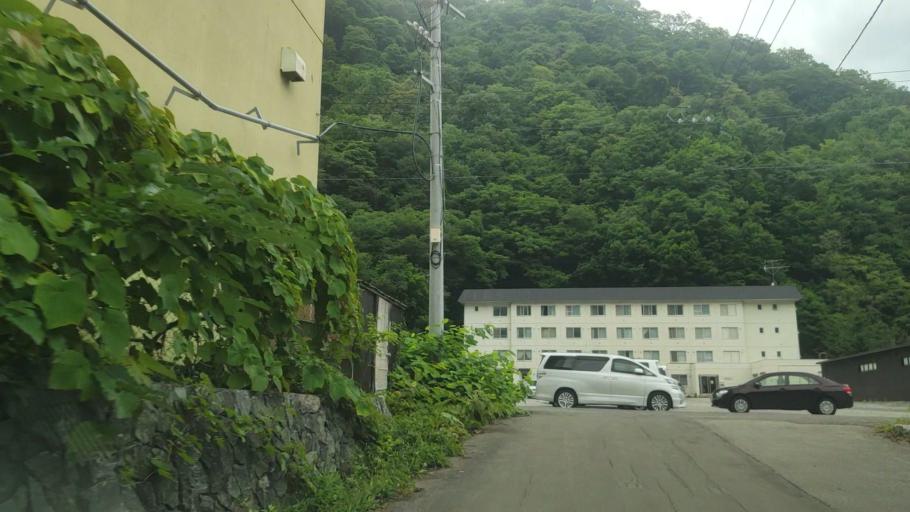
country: JP
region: Hokkaido
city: Sapporo
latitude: 42.9651
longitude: 141.1599
